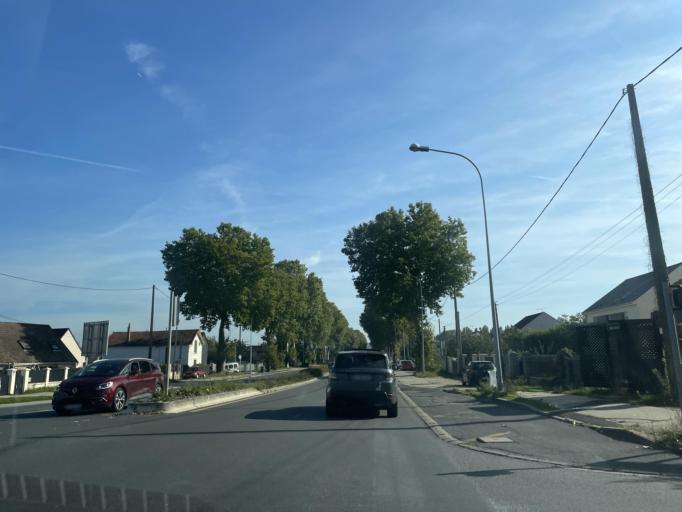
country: FR
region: Ile-de-France
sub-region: Departement de Seine-et-Marne
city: Trilport
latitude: 48.9573
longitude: 2.9318
